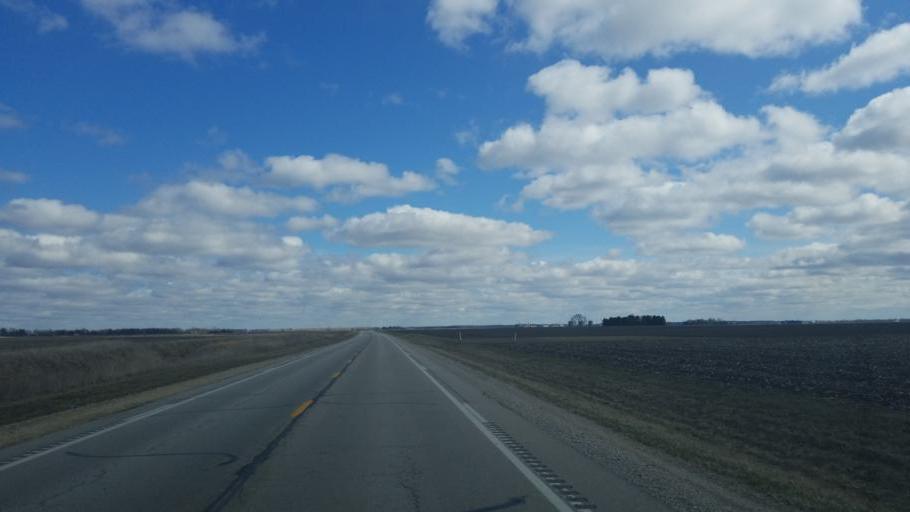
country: US
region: Illinois
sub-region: Douglas County
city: Villa Grove
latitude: 39.7919
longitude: -88.1118
